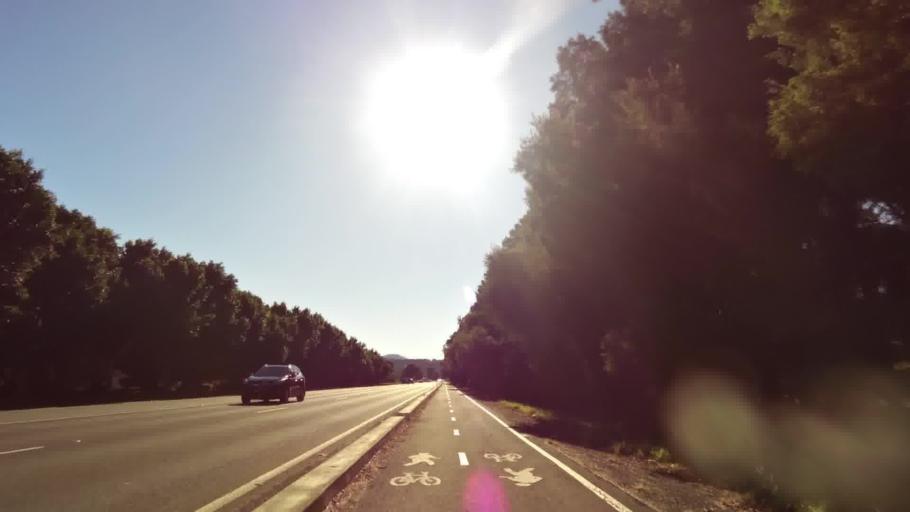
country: AU
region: New South Wales
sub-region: Wollongong
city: Koonawarra
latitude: -34.4862
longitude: 150.7998
